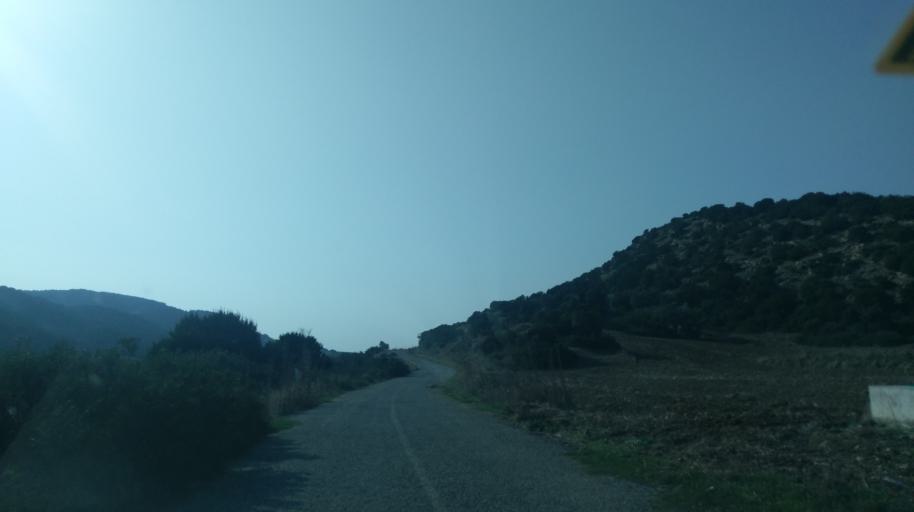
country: CY
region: Ammochostos
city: Rizokarpaso
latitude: 35.5539
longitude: 34.3672
